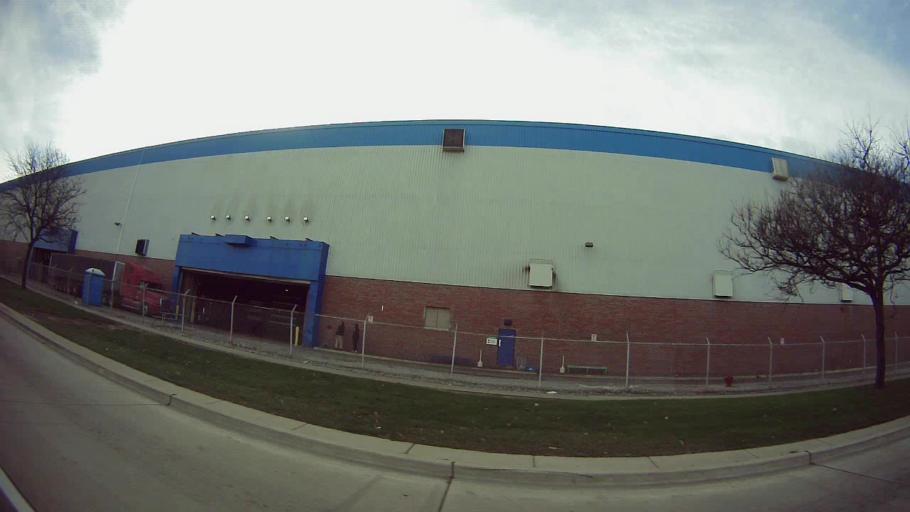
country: US
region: Michigan
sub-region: Macomb County
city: Warren
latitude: 42.4626
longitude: -83.0426
